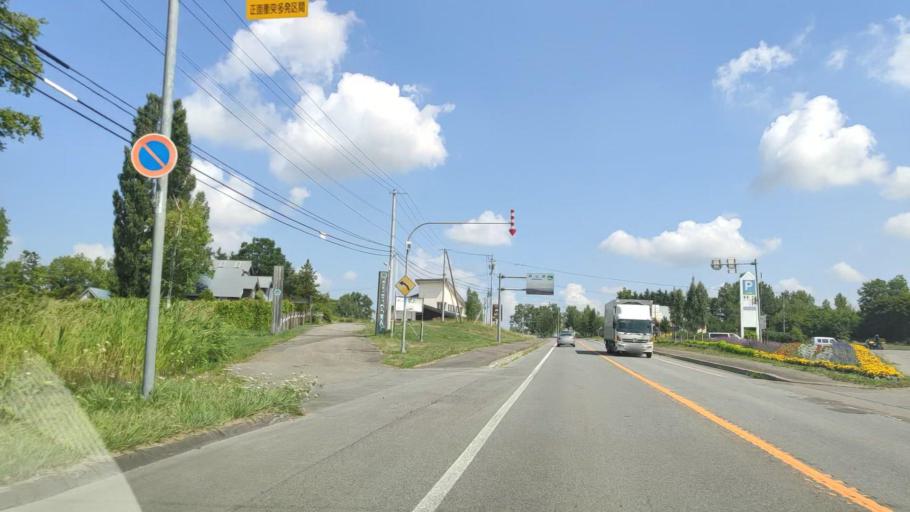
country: JP
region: Hokkaido
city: Shimo-furano
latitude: 43.5171
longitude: 142.4476
